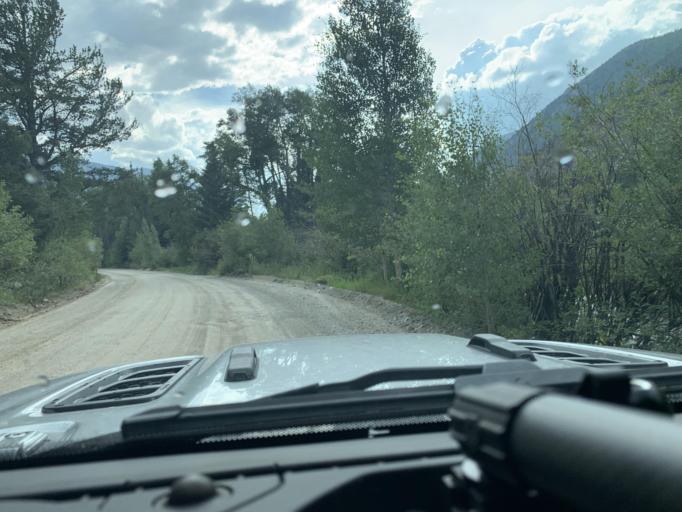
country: US
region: Colorado
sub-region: Chaffee County
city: Buena Vista
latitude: 38.7157
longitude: -106.2575
